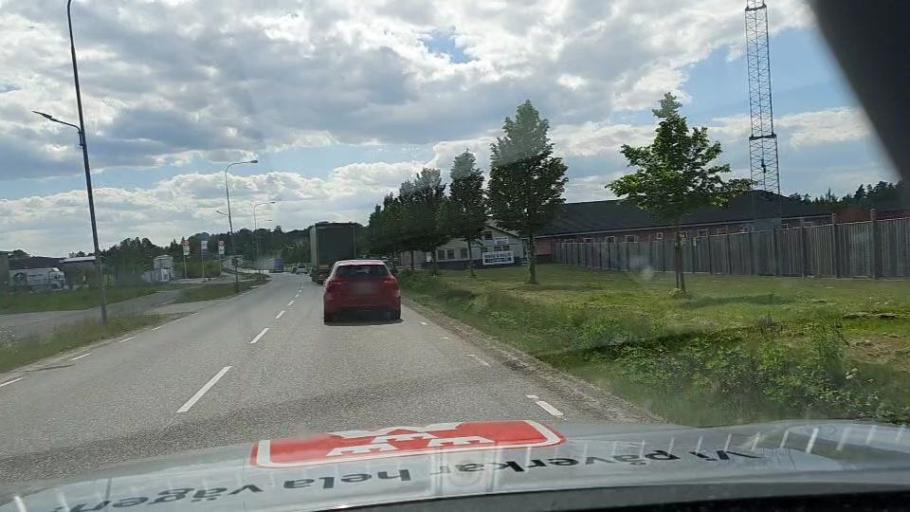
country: SE
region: Kronoberg
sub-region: Ljungby Kommun
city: Ljungby
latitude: 56.8474
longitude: 13.9232
